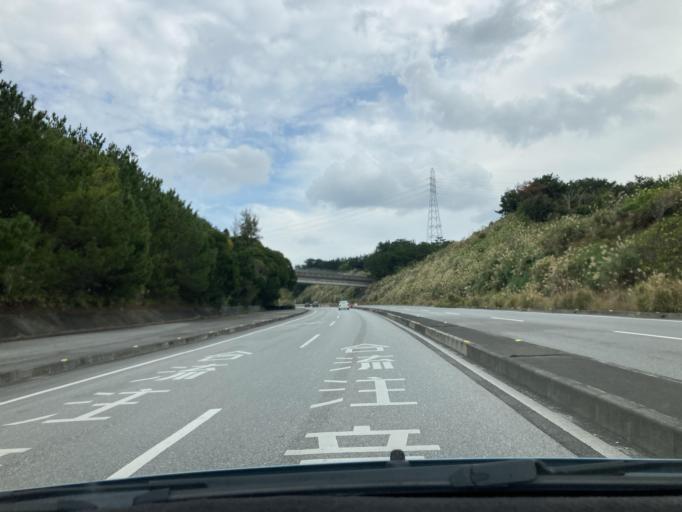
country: JP
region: Okinawa
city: Ishikawa
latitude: 26.4817
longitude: 127.8496
